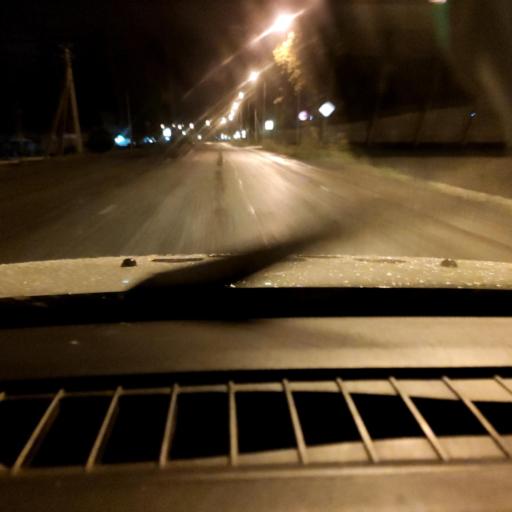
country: RU
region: Udmurtiya
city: Khokhryaki
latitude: 57.1854
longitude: 53.1547
